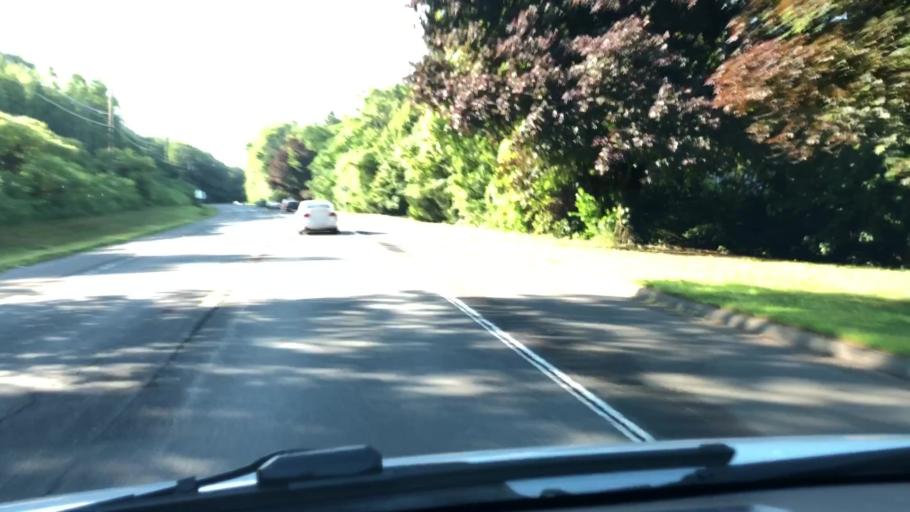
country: US
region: Massachusetts
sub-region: Hampshire County
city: North Amherst
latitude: 42.4434
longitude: -72.5527
